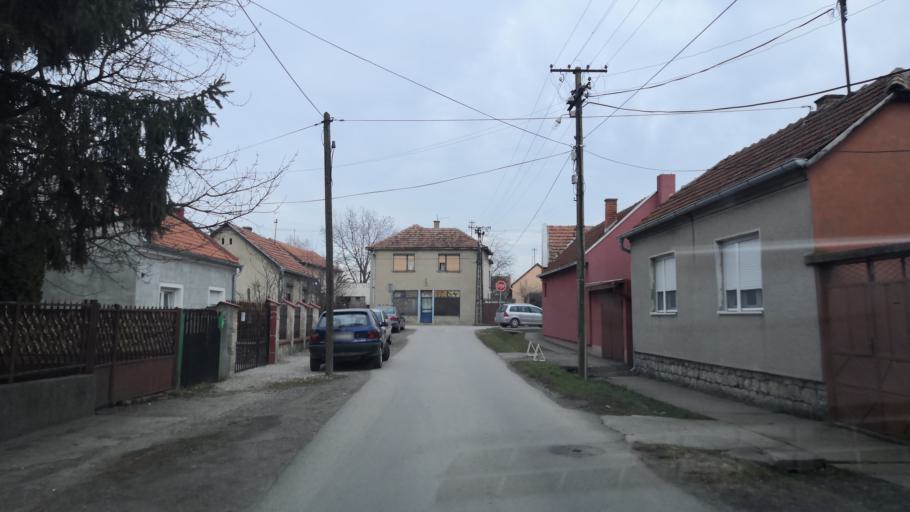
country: RS
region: Autonomna Pokrajina Vojvodina
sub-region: Sremski Okrug
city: Ingija
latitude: 45.0548
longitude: 20.0847
